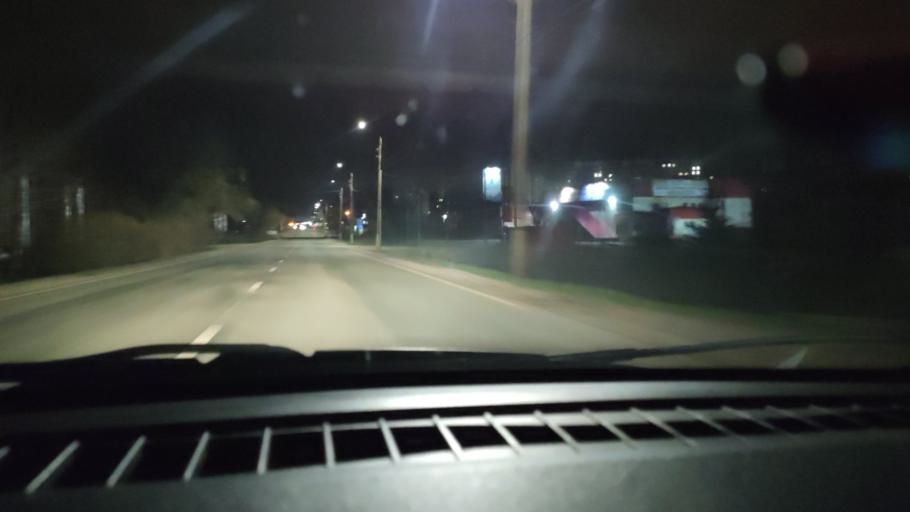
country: RU
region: Bashkortostan
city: Sterlitamak
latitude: 53.6435
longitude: 55.8931
